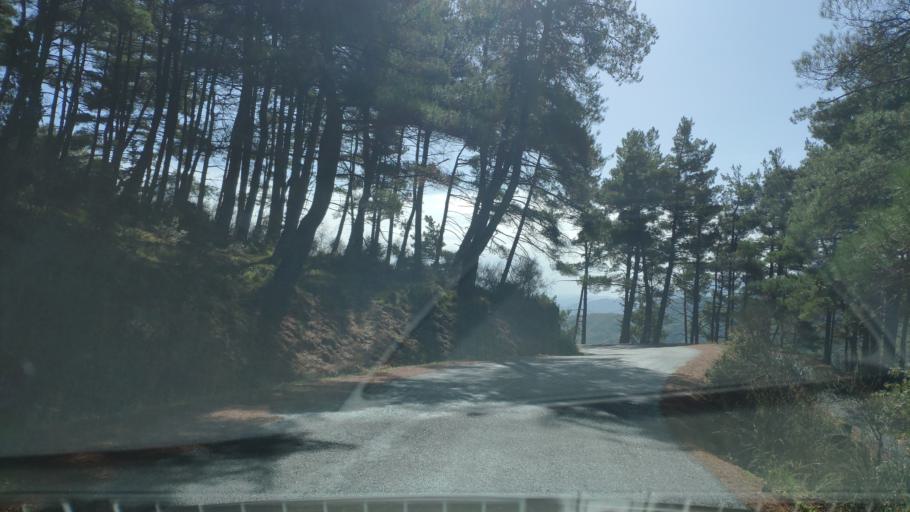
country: GR
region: Peloponnese
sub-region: Nomos Arkadias
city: Dimitsana
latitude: 37.5894
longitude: 22.0431
